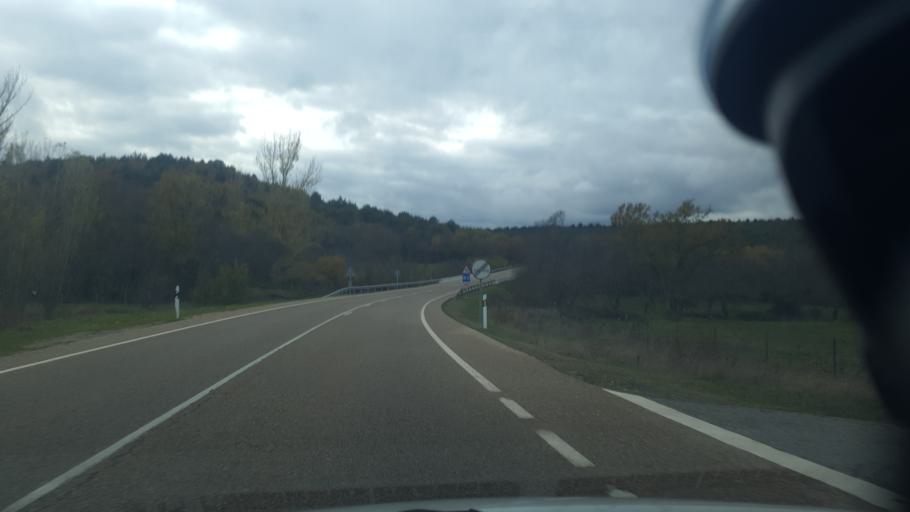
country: ES
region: Castille and Leon
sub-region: Provincia de Segovia
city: Casla
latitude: 41.1859
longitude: -3.6217
